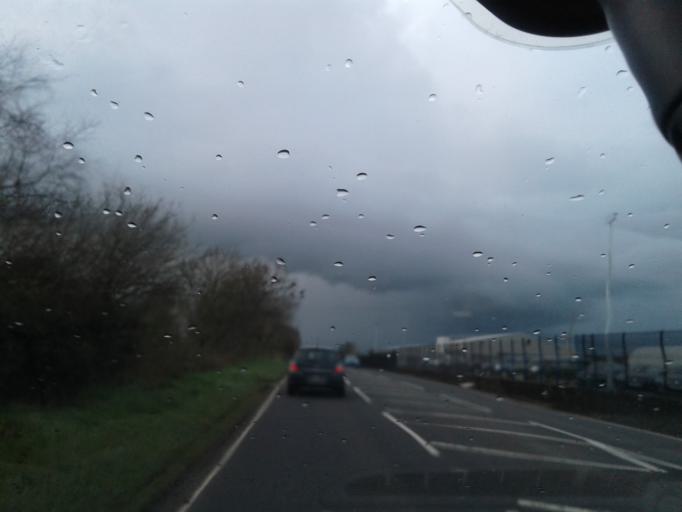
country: GB
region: Northern Ireland
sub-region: Strabane District
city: Sion Mills
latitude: 54.7556
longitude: -7.4508
